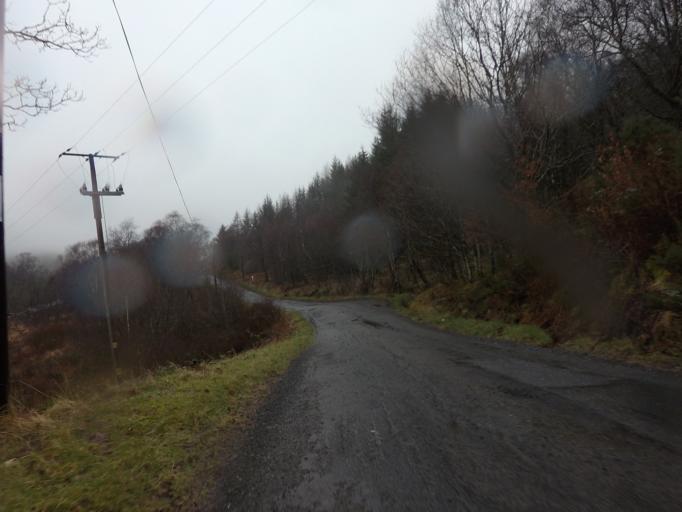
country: GB
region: Scotland
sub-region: West Dunbartonshire
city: Balloch
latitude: 56.1984
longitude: -4.5239
